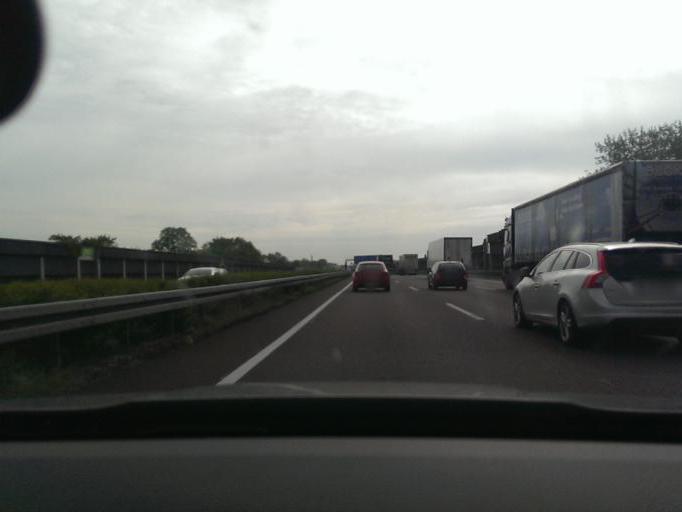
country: DE
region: Lower Saxony
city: Lehre
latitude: 52.3098
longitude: 10.6108
